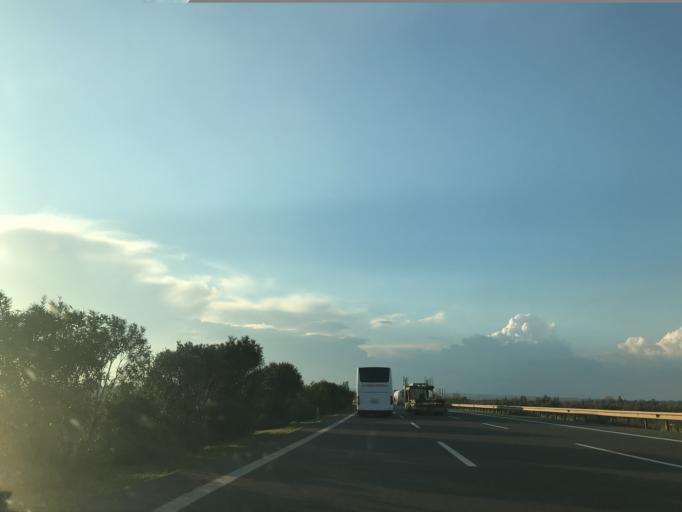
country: TR
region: Adana
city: Ceyhan
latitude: 37.0011
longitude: 35.7291
